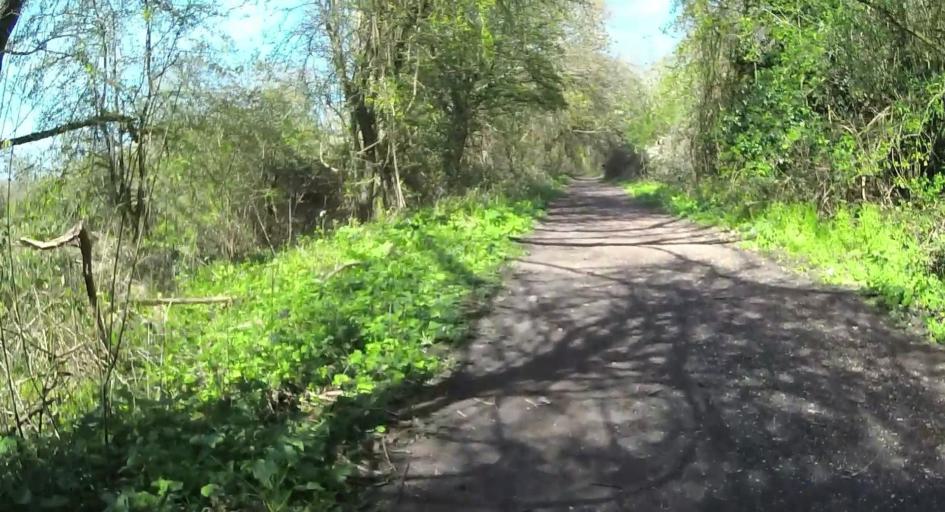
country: GB
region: England
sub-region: Hampshire
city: Romsey
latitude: 51.0796
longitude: -1.5026
